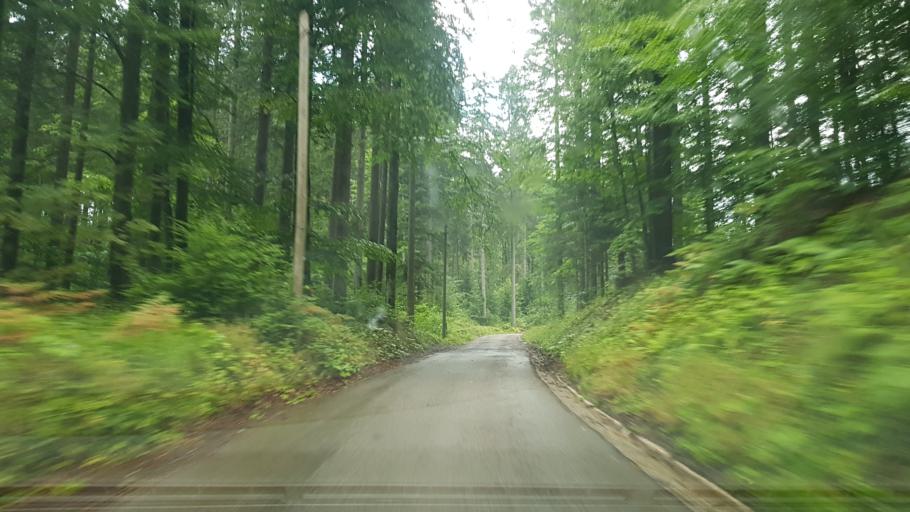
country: IT
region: Friuli Venezia Giulia
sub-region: Provincia di Udine
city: Tarvisio
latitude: 46.4887
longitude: 13.6087
